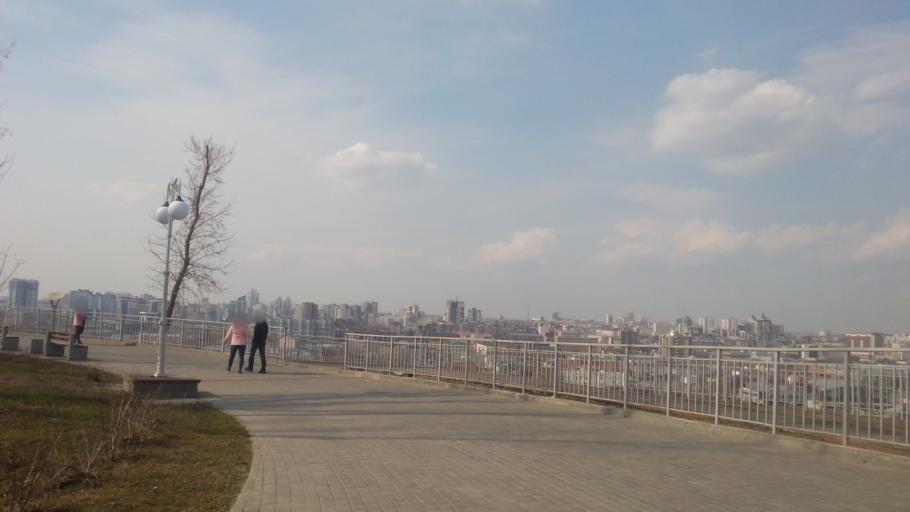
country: RU
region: Altai Krai
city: Zaton
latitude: 53.3245
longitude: 83.7958
